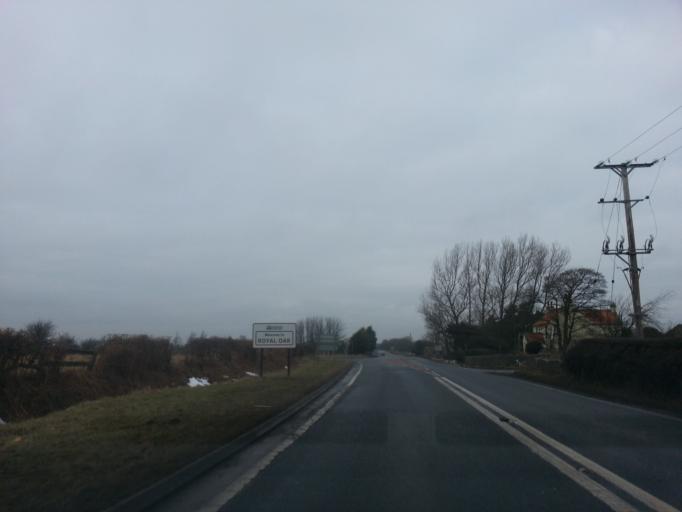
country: GB
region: England
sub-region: Darlington
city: Summerhouse
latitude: 54.6061
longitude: -1.6791
